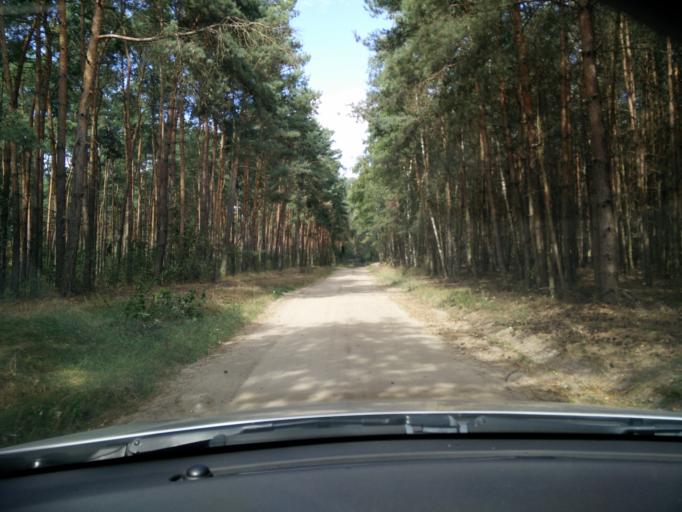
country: PL
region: Greater Poland Voivodeship
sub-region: Powiat sredzki
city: Sroda Wielkopolska
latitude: 52.2826
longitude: 17.2427
